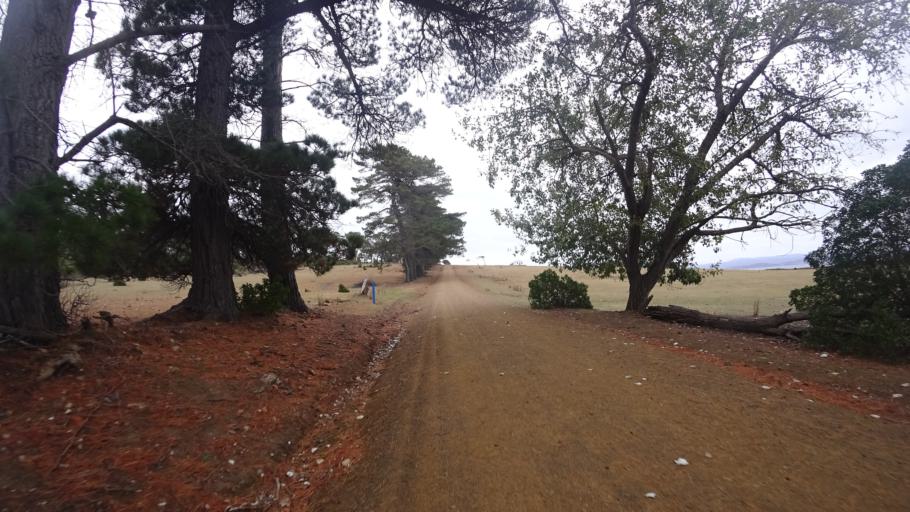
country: AU
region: Tasmania
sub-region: Sorell
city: Sorell
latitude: -42.5828
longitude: 148.0632
